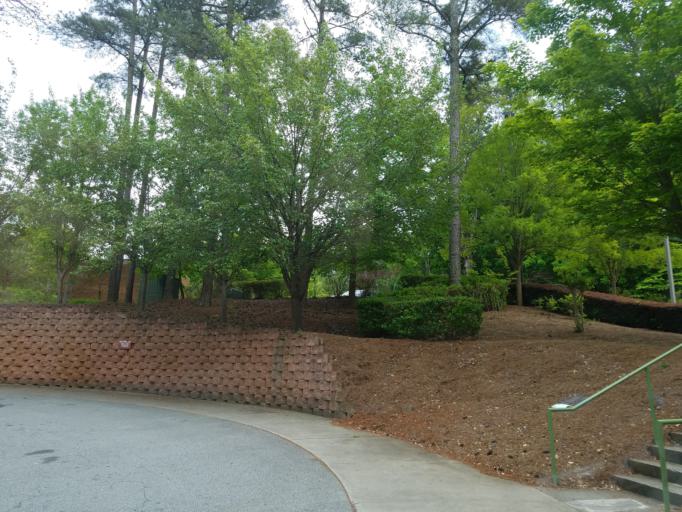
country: US
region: Georgia
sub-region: Cobb County
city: Fair Oaks
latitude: 33.9310
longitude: -84.5182
